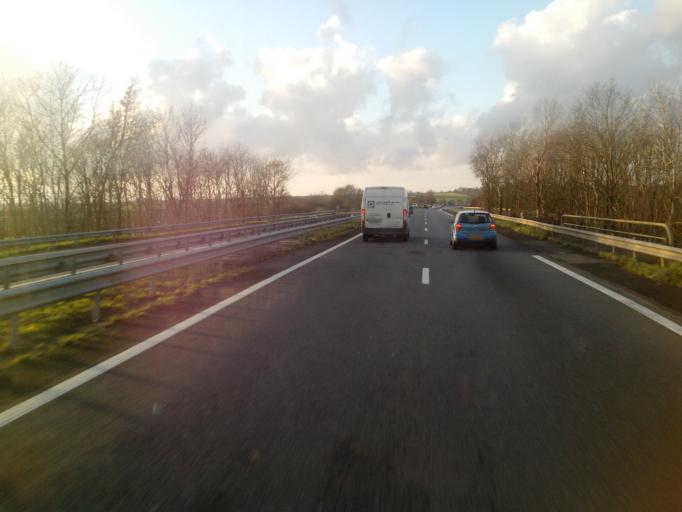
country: FR
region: Pays de la Loire
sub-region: Departement de Maine-et-Loire
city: Tillieres
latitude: 47.1388
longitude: -1.1647
